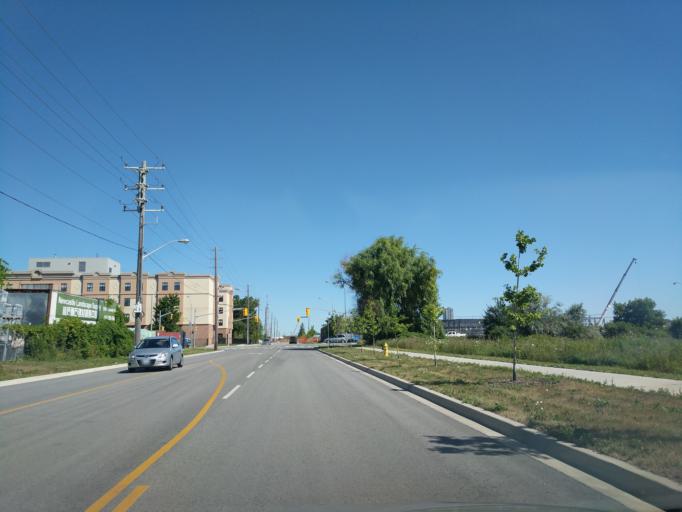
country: CA
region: Ontario
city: Scarborough
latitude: 43.8120
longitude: -79.2989
